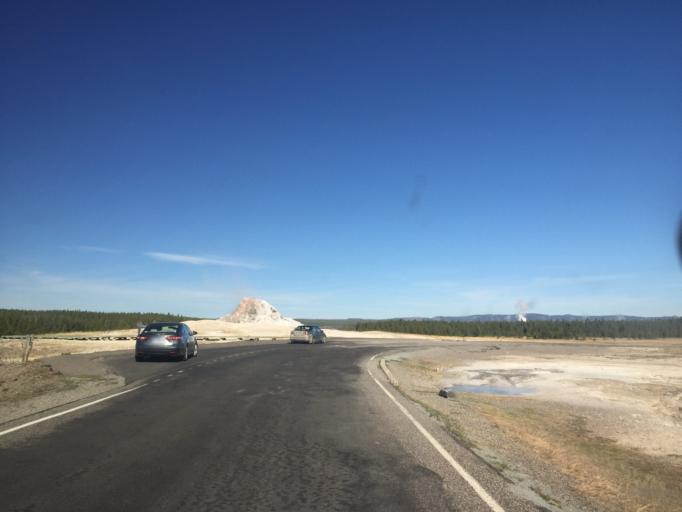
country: US
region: Montana
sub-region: Gallatin County
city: West Yellowstone
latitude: 44.5387
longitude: -110.8019
